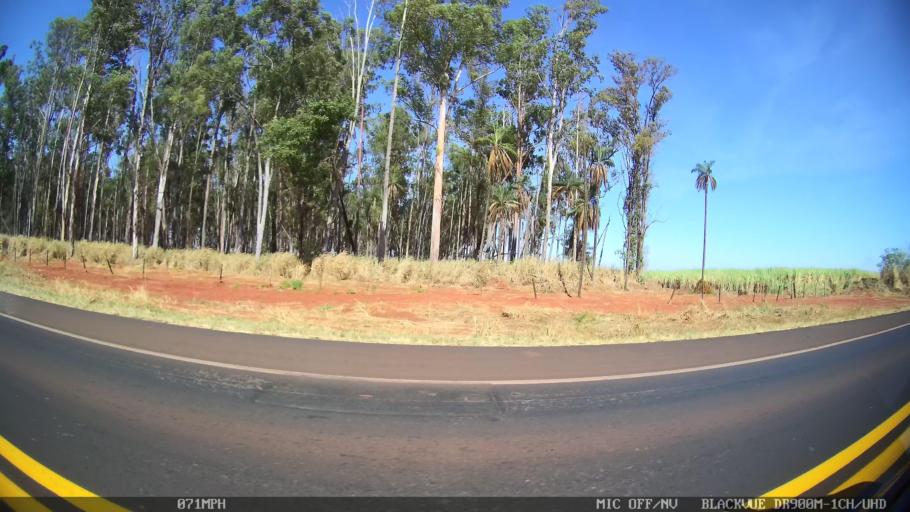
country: BR
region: Sao Paulo
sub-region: Barretos
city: Barretos
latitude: -20.4941
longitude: -48.5284
